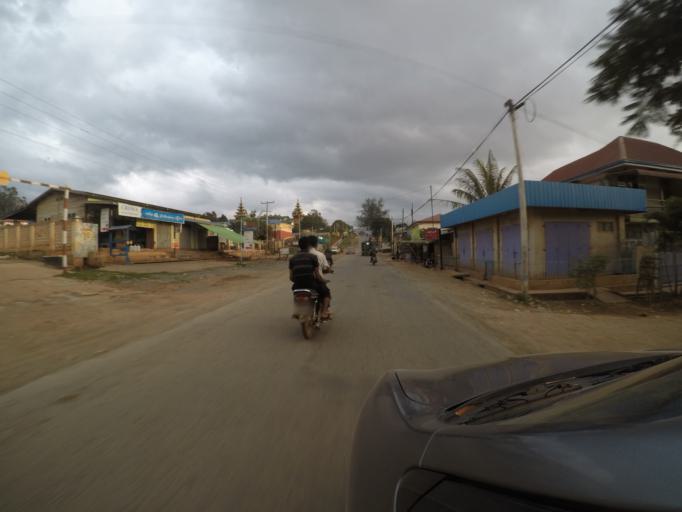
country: MM
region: Shan
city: Taunggyi
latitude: 20.7815
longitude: 96.9970
